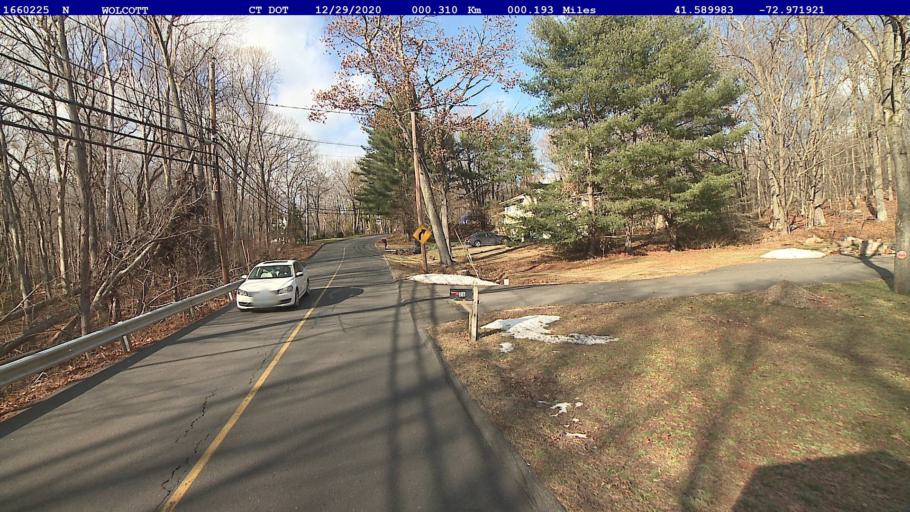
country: US
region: Connecticut
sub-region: New Haven County
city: Wolcott
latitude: 41.5900
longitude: -72.9719
